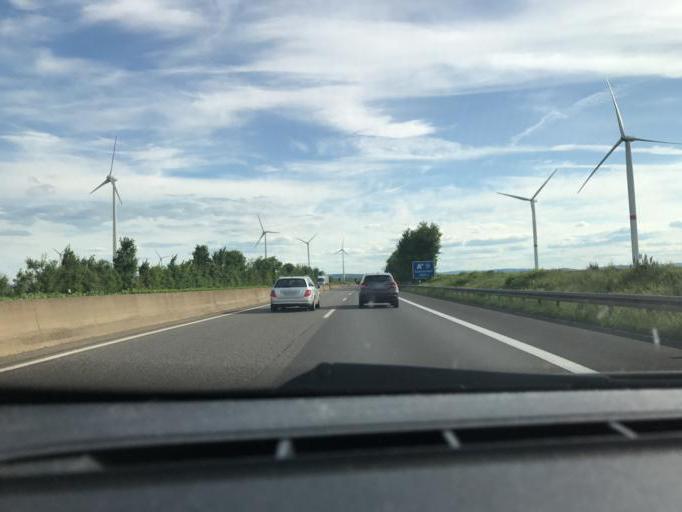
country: DE
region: North Rhine-Westphalia
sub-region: Regierungsbezirk Koln
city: Euskirchen
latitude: 50.6997
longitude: 6.7699
